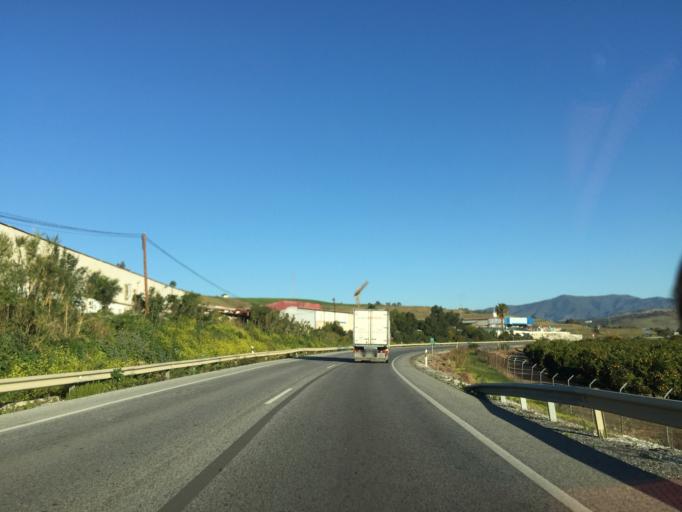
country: ES
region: Andalusia
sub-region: Provincia de Malaga
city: Pizarra
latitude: 36.7585
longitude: -4.7287
